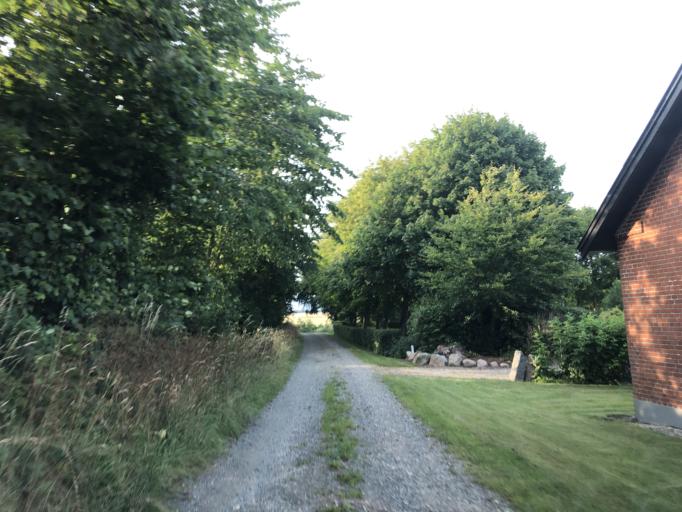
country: DK
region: South Denmark
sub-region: Fredericia Kommune
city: Taulov
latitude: 55.5868
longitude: 9.6142
